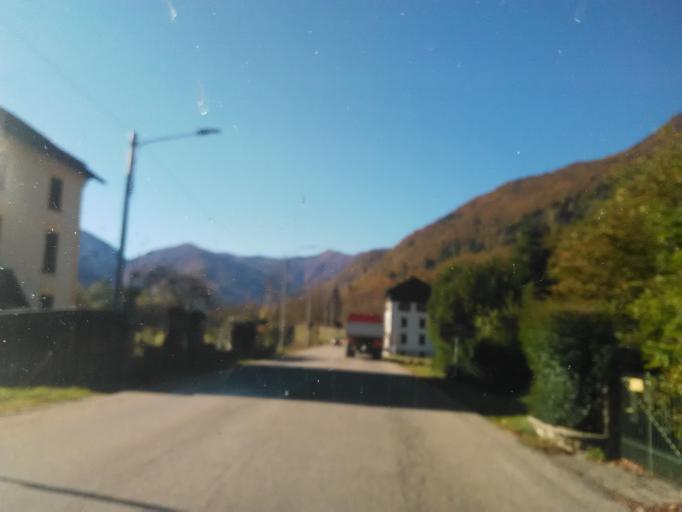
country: IT
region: Piedmont
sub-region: Provincia di Vercelli
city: Scopa
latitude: 45.8056
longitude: 8.1224
